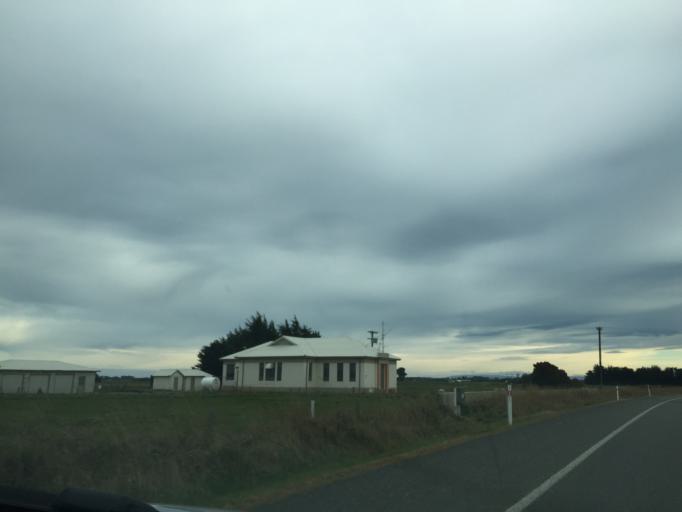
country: NZ
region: Southland
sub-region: Invercargill City
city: Invercargill
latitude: -46.3189
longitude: 168.6229
